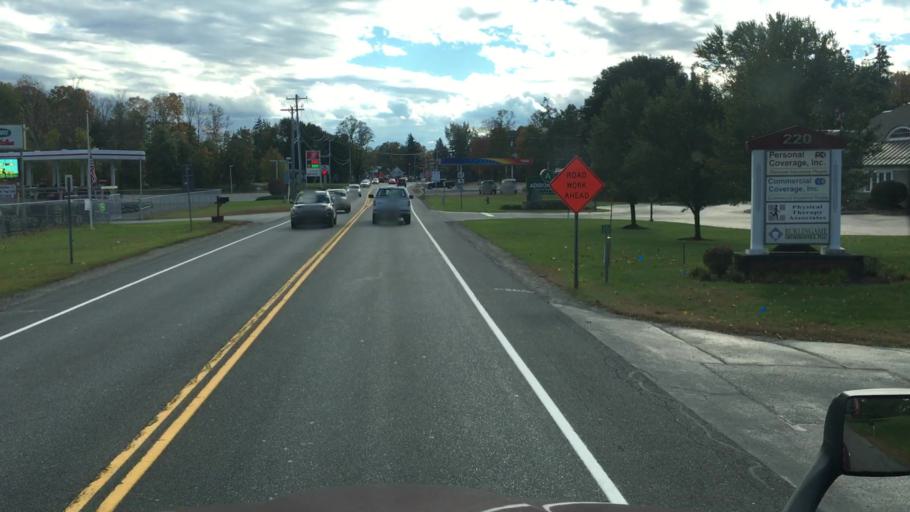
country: US
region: New York
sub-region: Saratoga County
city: Ballston Spa
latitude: 42.9907
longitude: -73.8515
